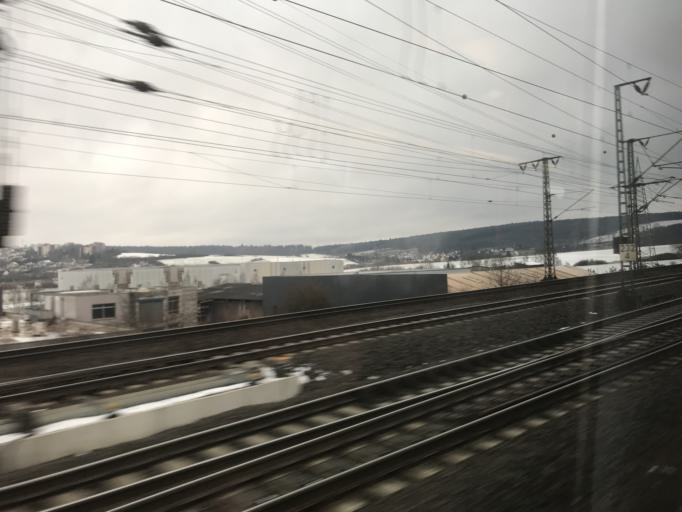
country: DE
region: Hesse
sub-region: Regierungsbezirk Kassel
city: Fulda
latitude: 50.5678
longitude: 9.6842
